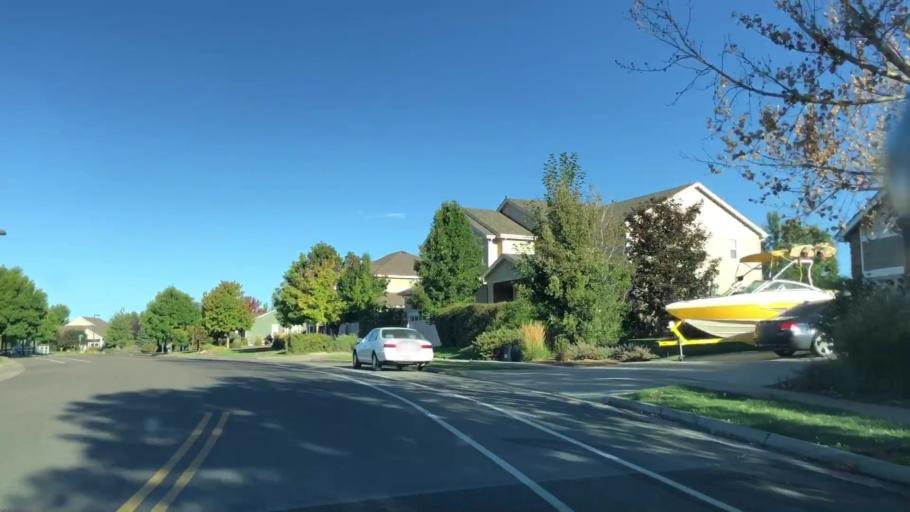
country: US
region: Colorado
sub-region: Larimer County
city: Loveland
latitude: 40.4610
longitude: -105.0331
